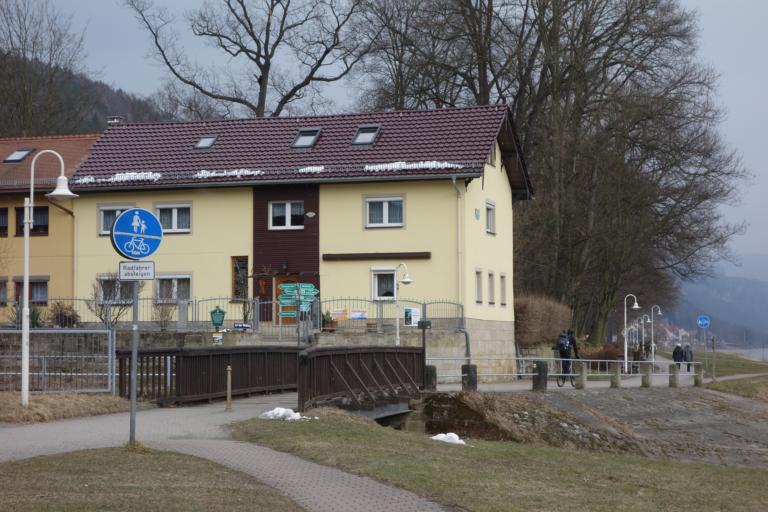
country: DE
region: Saxony
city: Bad Schandau
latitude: 50.9156
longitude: 14.1581
